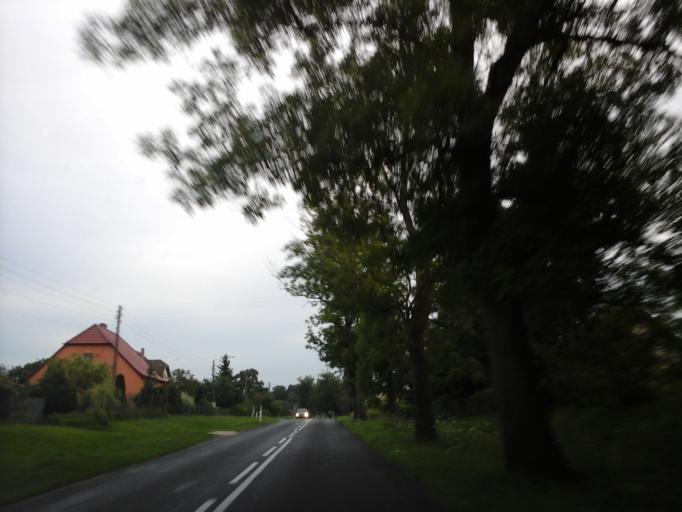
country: PL
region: West Pomeranian Voivodeship
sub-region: Powiat goleniowski
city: Maszewo
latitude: 53.5426
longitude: 15.1235
